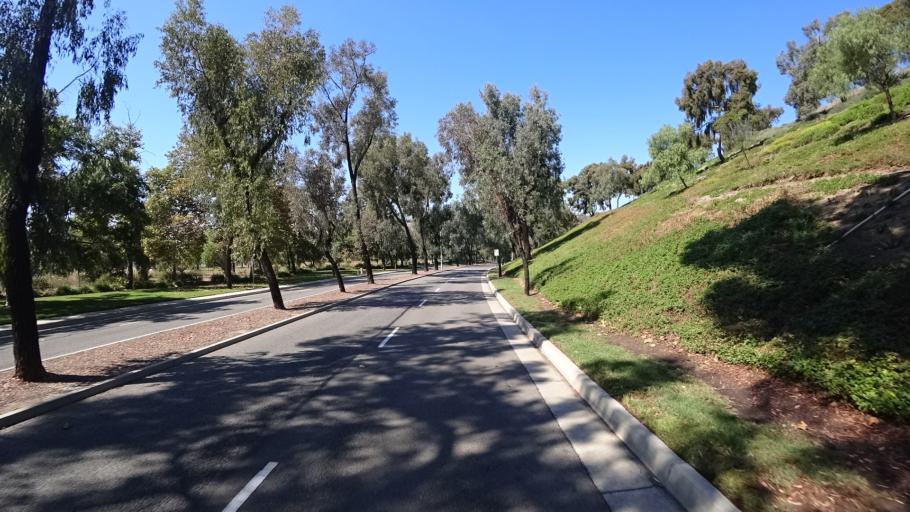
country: US
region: California
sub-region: Orange County
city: San Clemente
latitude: 33.4429
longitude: -117.6105
